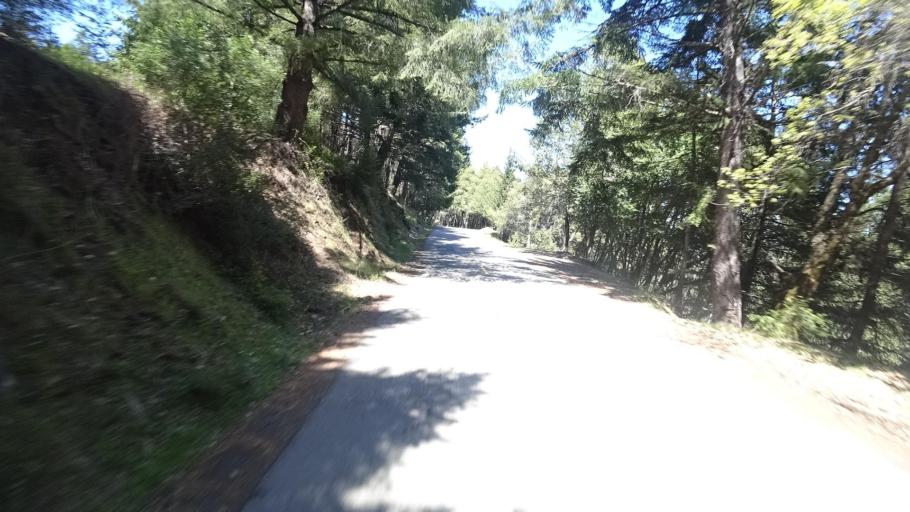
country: US
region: California
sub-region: Humboldt County
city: Rio Dell
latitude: 40.2971
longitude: -124.0566
